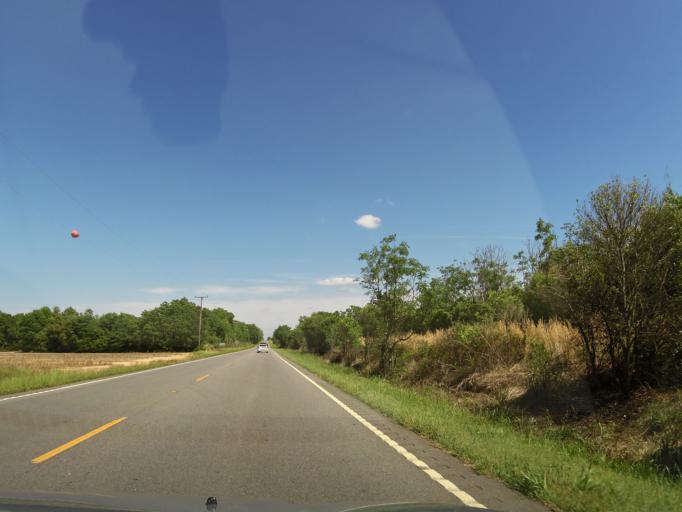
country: US
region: South Carolina
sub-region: Aiken County
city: Aiken
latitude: 33.5260
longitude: -81.6280
